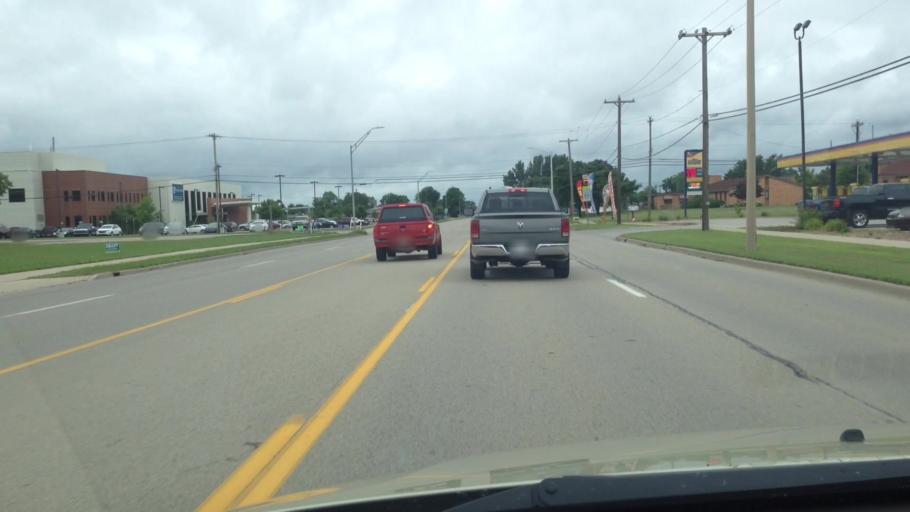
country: US
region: Michigan
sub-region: Delta County
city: Escanaba
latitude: 45.7345
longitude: -87.0799
